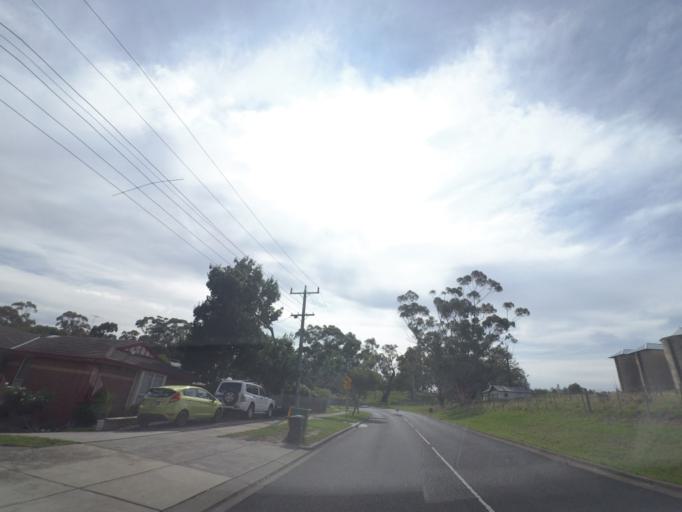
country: AU
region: Victoria
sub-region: Banyule
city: Viewbank
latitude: -37.7439
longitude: 145.0940
